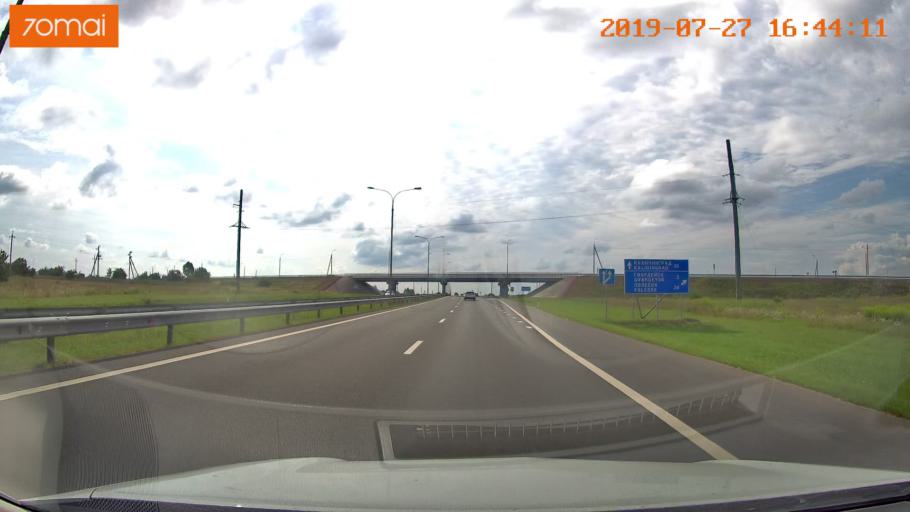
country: RU
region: Kaliningrad
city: Gvardeysk
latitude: 54.6726
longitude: 21.0827
